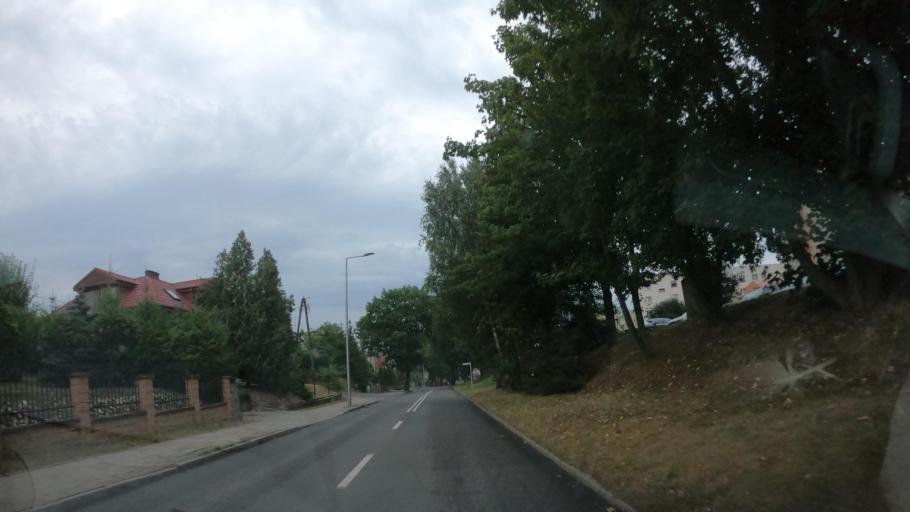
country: PL
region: Lubusz
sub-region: Powiat krosnienski
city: Krosno Odrzanskie
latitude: 52.0565
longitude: 15.1095
